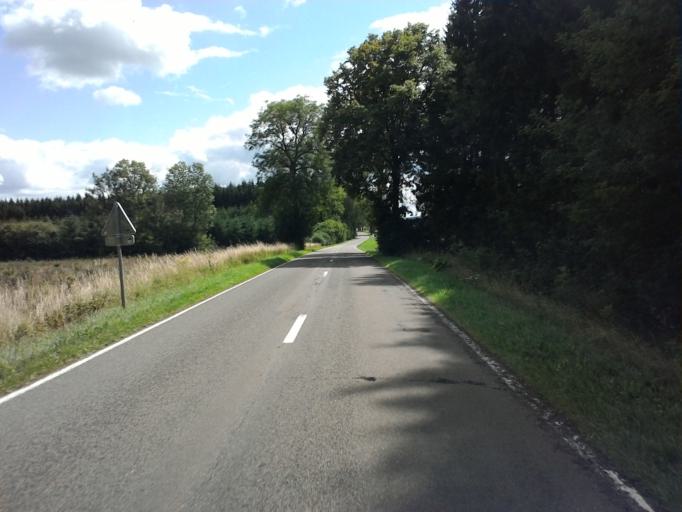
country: BE
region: Wallonia
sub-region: Province du Luxembourg
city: Leglise
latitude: 49.7900
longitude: 5.5878
